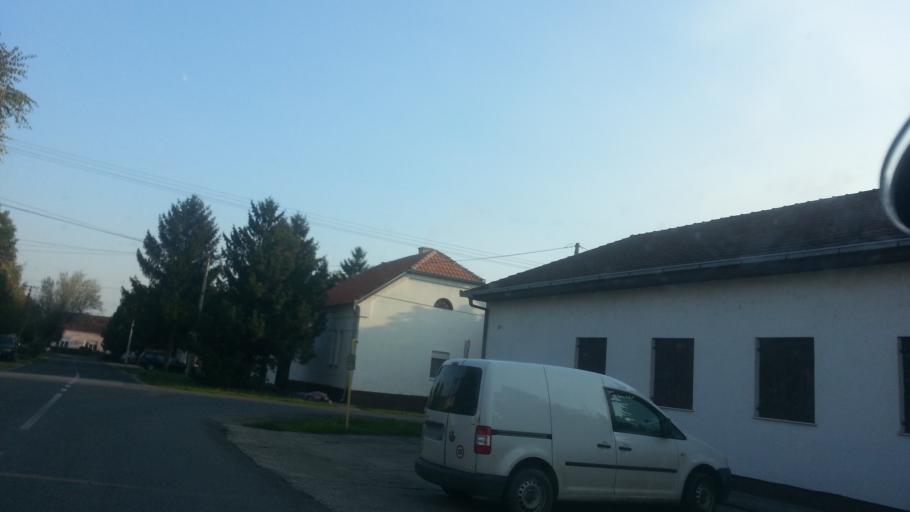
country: RS
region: Autonomna Pokrajina Vojvodina
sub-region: Sremski Okrug
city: Ingija
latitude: 45.0485
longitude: 20.0868
